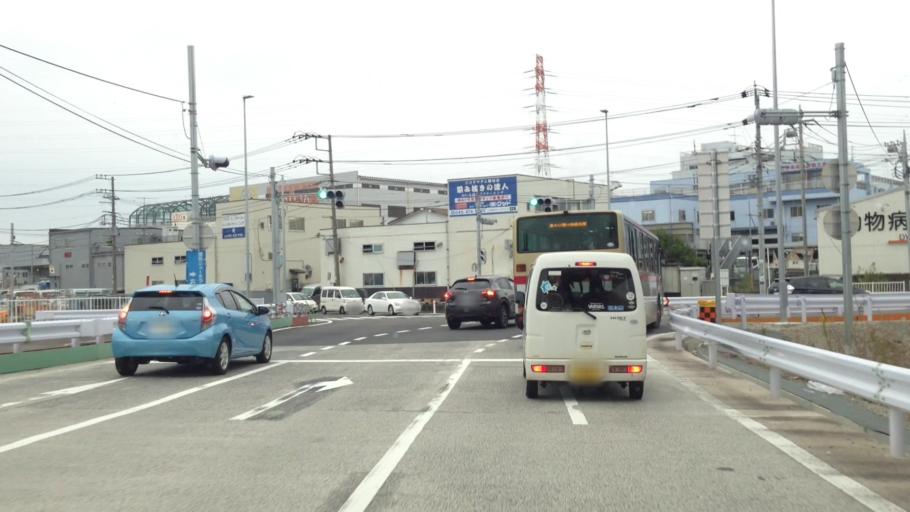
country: JP
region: Kanagawa
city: Yokohama
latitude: 35.5164
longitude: 139.5900
